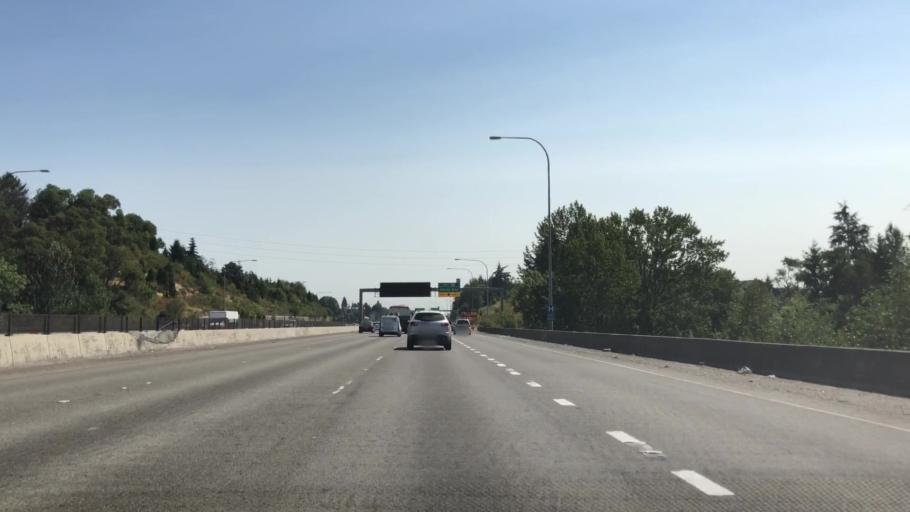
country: US
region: Washington
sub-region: Pierce County
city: Fircrest
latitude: 47.2346
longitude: -122.4926
